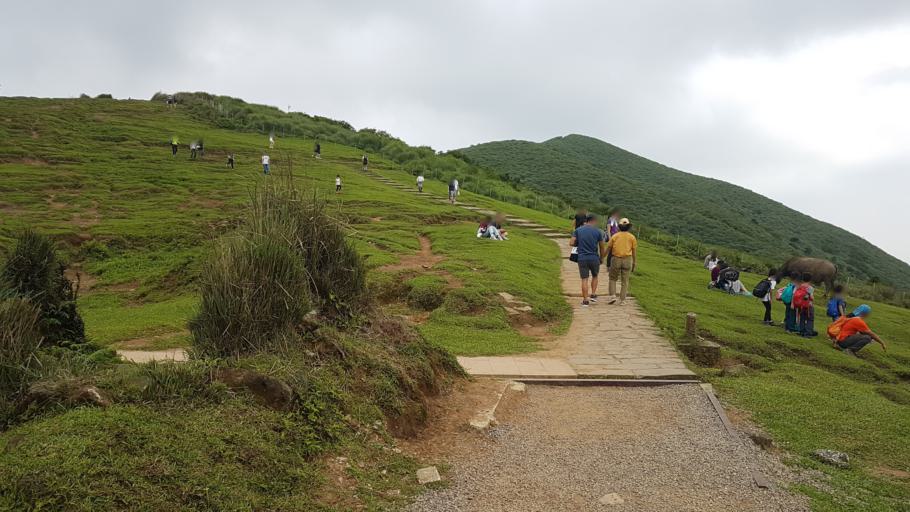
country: TW
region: Taipei
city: Taipei
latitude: 25.1623
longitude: 121.5745
